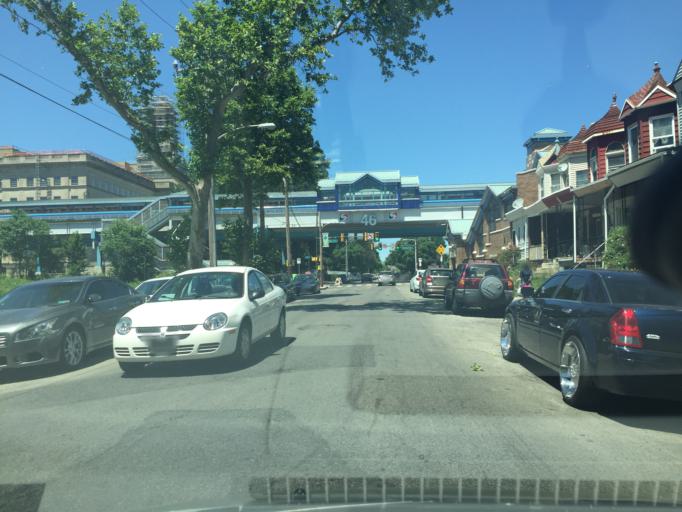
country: US
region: Pennsylvania
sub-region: Delaware County
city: Millbourne
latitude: 39.9579
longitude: -75.2142
